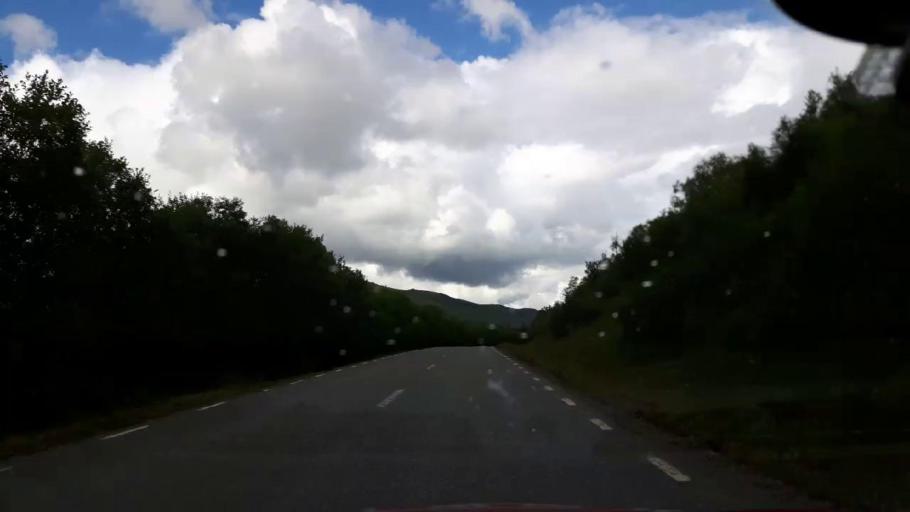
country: NO
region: Nordland
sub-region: Hattfjelldal
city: Hattfjelldal
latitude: 65.0707
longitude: 14.6551
